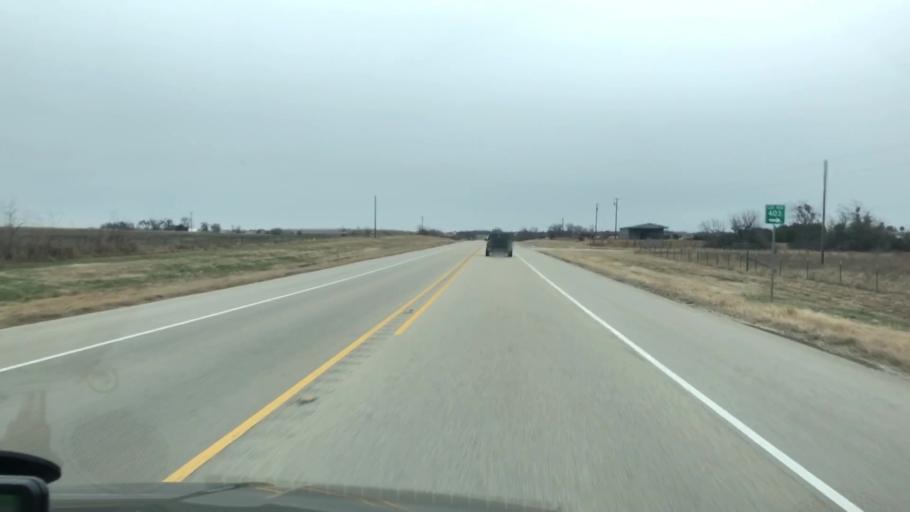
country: US
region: Texas
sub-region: Hamilton County
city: Hamilton
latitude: 31.6376
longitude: -98.1506
